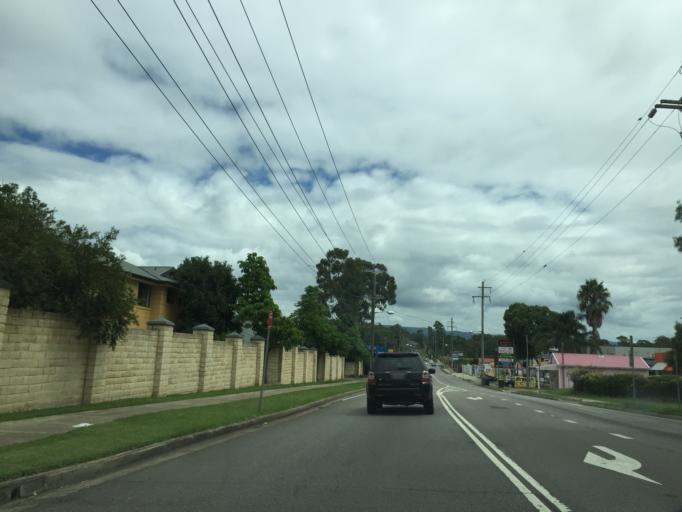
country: AU
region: New South Wales
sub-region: Hawkesbury
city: Richmond
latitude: -33.5797
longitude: 150.7194
